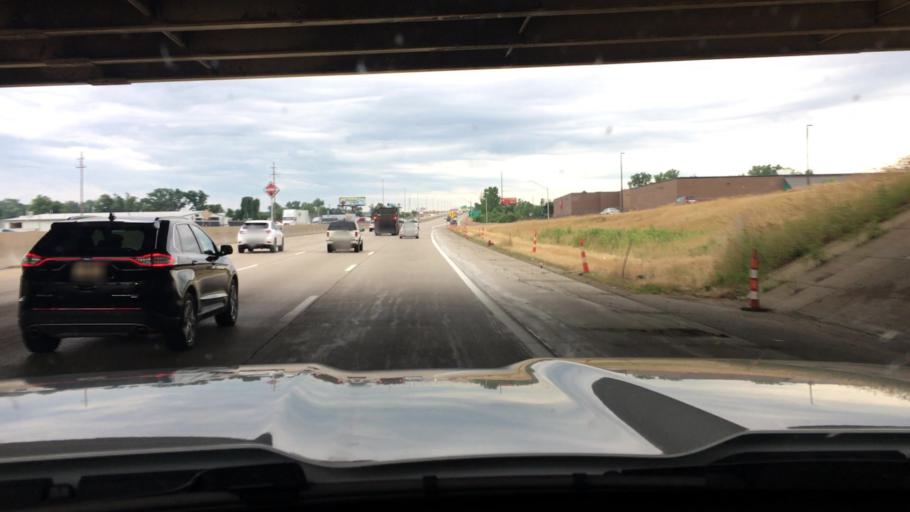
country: US
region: Michigan
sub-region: Kent County
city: Cutlerville
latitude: 42.8660
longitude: -85.6797
